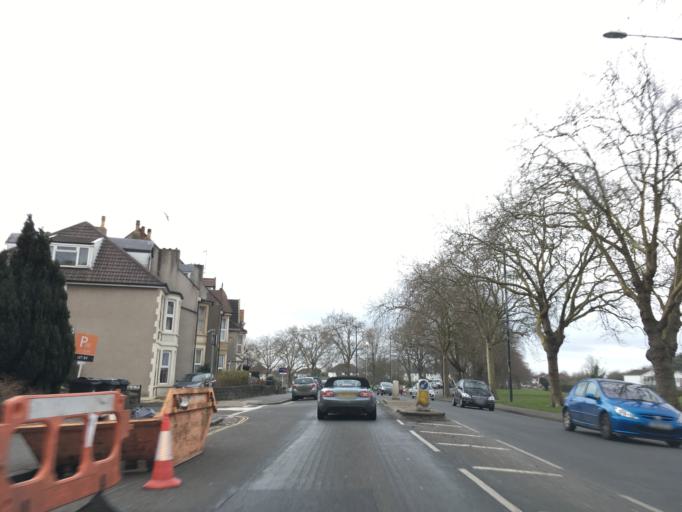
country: GB
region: England
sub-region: Bristol
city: Bristol
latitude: 51.4917
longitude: -2.5842
